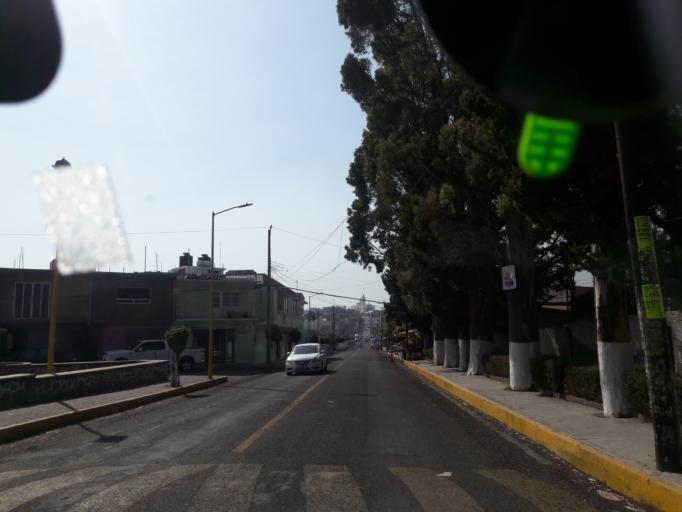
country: MX
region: Tlaxcala
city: Panotla
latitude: 19.3186
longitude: -98.2717
